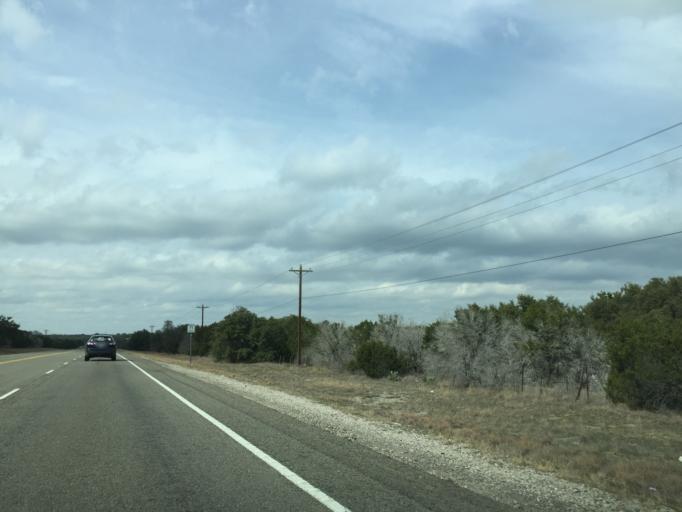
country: US
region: Texas
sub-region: Burnet County
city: Meadowlakes
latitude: 30.4948
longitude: -98.2524
